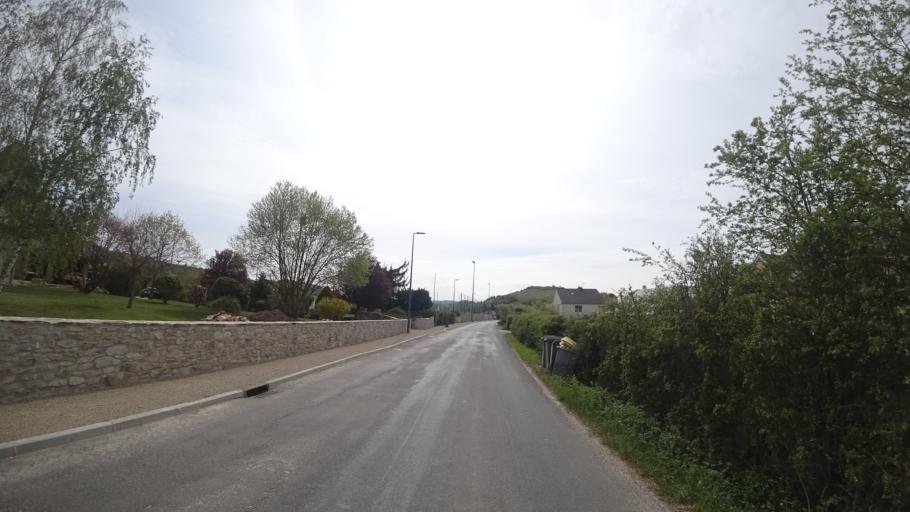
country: FR
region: Midi-Pyrenees
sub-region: Departement de l'Aveyron
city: Sebazac-Concoures
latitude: 44.3781
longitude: 2.6049
